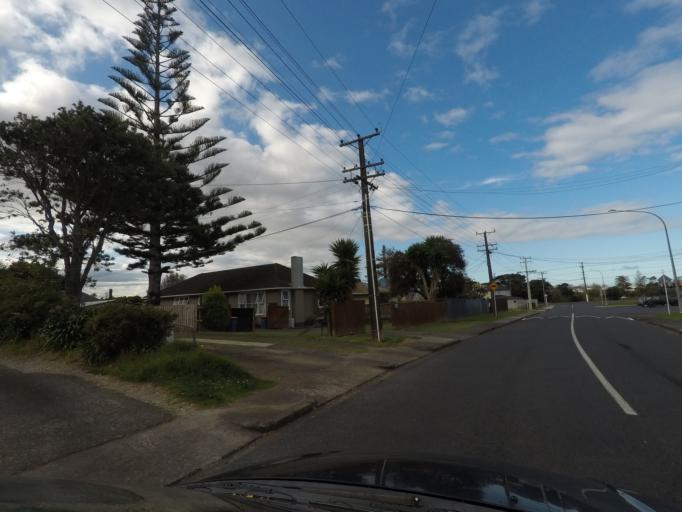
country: NZ
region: Auckland
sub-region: Auckland
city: Rosebank
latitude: -36.8843
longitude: 174.6564
